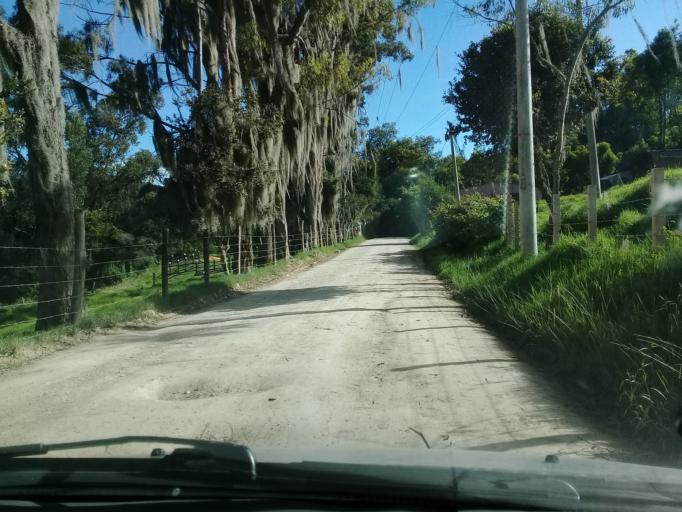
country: CO
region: Cundinamarca
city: Tabio
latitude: 4.9627
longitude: -74.0803
